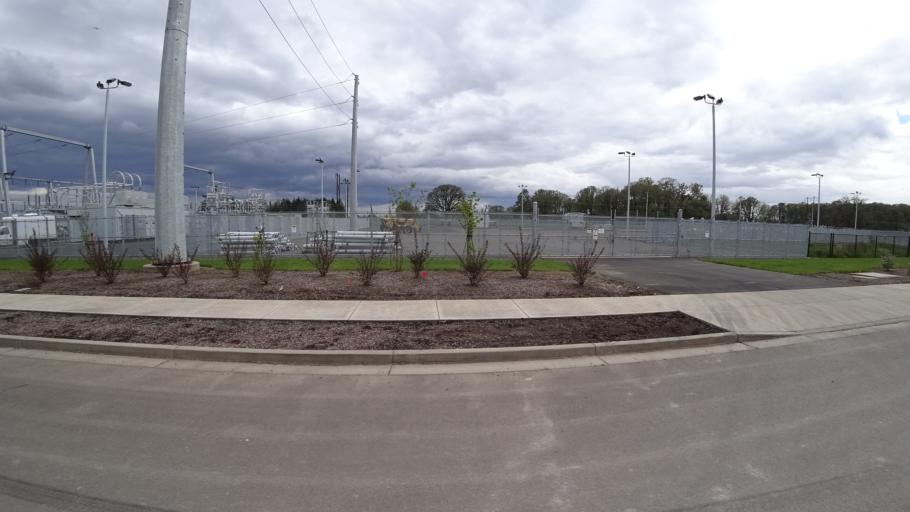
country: US
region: Oregon
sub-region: Washington County
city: Hillsboro
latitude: 45.5586
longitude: -122.9394
